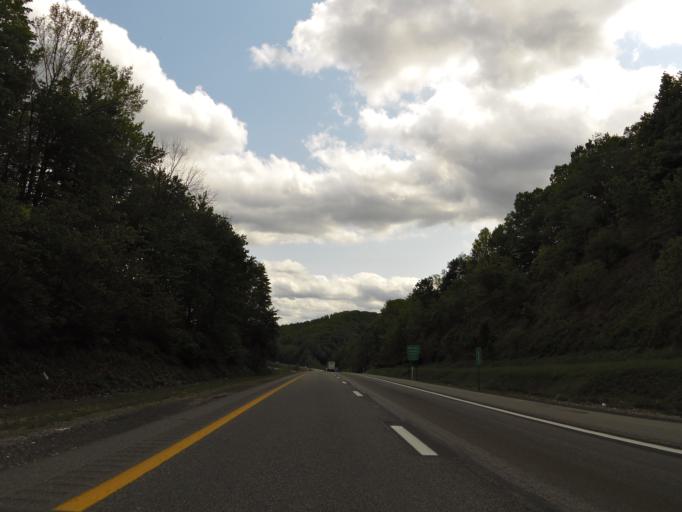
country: US
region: West Virginia
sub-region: Raleigh County
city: Bradley
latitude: 37.8880
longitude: -81.2674
